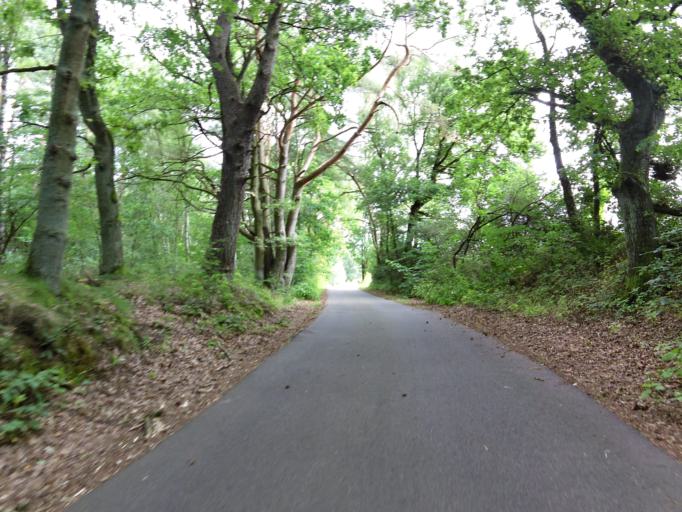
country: DE
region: Brandenburg
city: Lychen
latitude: 53.2318
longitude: 13.2816
